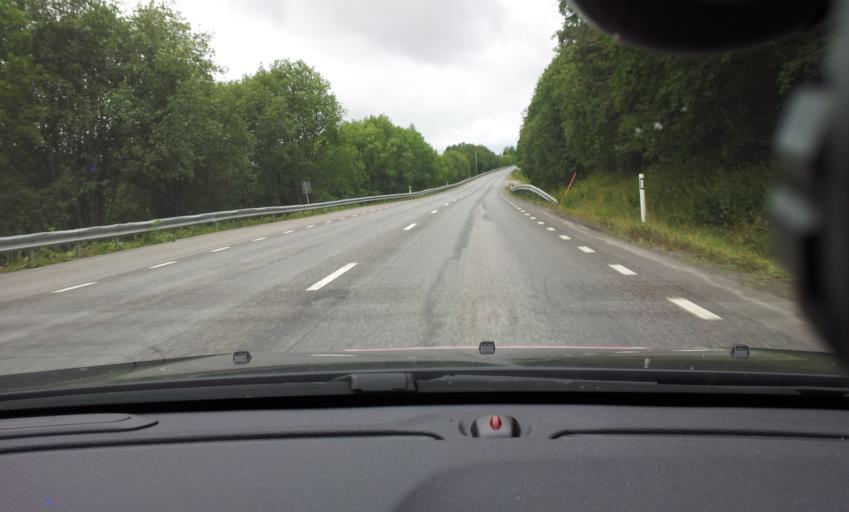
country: SE
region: Jaemtland
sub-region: Are Kommun
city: Are
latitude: 63.3960
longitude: 12.9573
